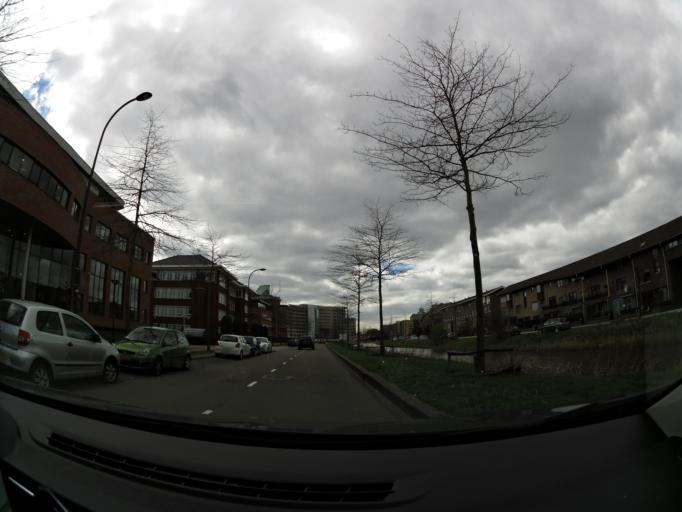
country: NL
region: South Holland
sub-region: Gemeente Rotterdam
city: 's-Gravenland
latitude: 51.9166
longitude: 4.5510
